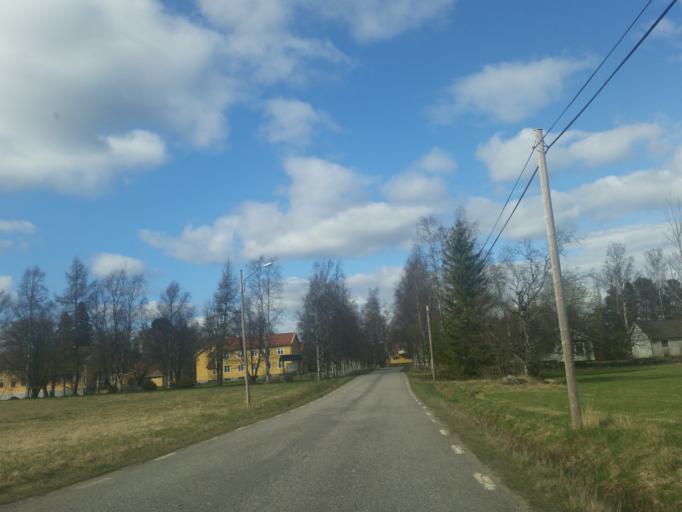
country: SE
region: Vaesterbotten
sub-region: Robertsfors Kommun
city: Robertsfors
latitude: 64.0429
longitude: 20.8583
